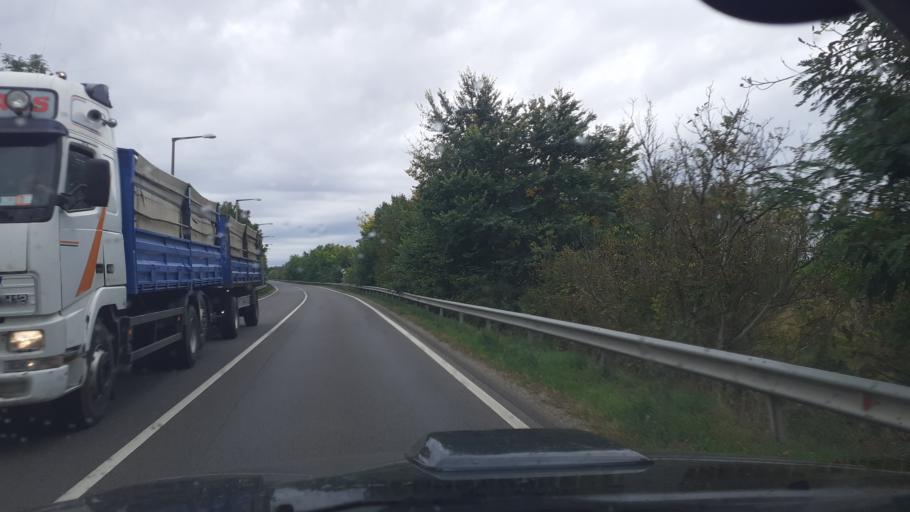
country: HU
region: Tolna
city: Dunafoldvar
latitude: 46.8032
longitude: 18.9279
